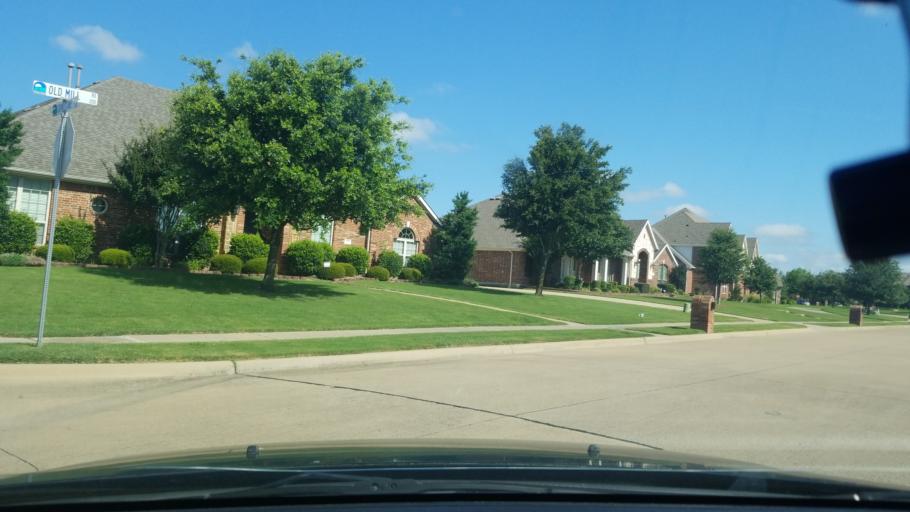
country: US
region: Texas
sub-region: Dallas County
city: Sunnyvale
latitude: 32.8041
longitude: -96.5828
